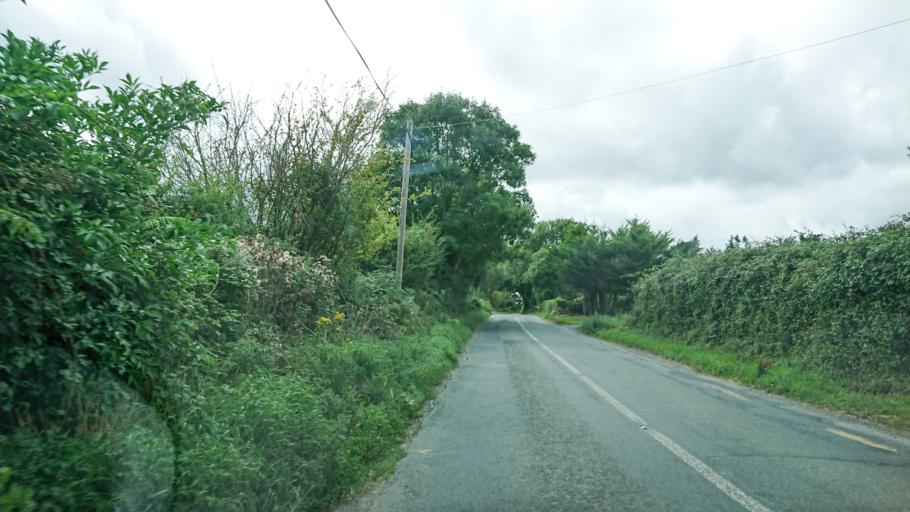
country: IE
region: Munster
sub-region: County Cork
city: Mallow
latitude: 52.1523
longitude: -8.5417
